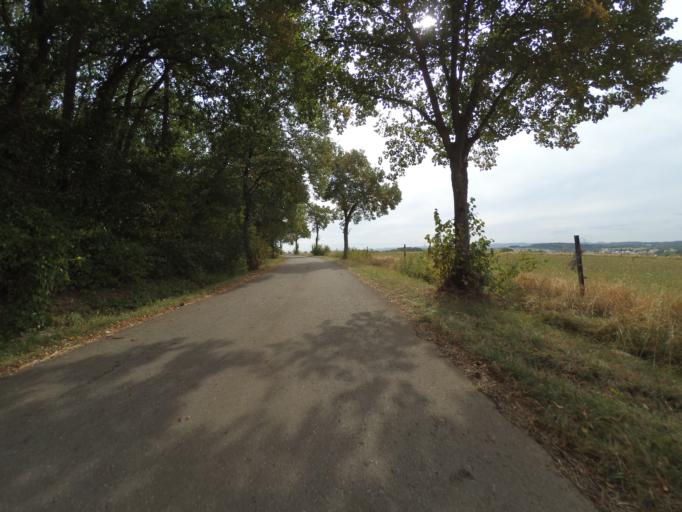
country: LU
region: Grevenmacher
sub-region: Canton de Remich
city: Mondorf-les-Bains
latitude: 49.5077
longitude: 6.2982
